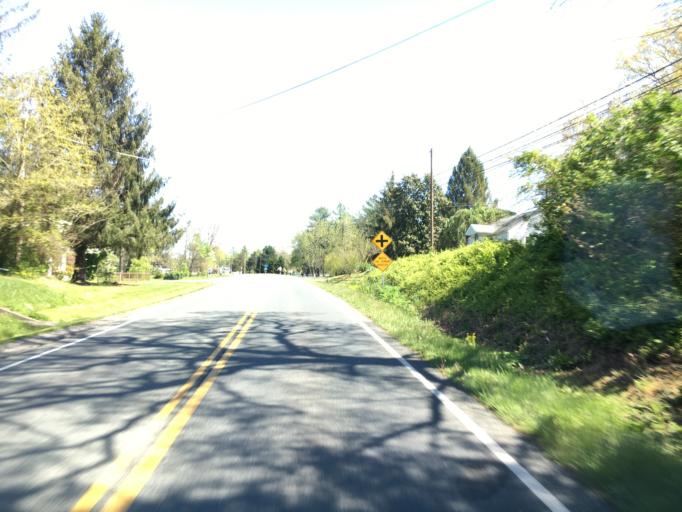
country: US
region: Virginia
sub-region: Augusta County
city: Crimora
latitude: 38.1466
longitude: -78.8410
